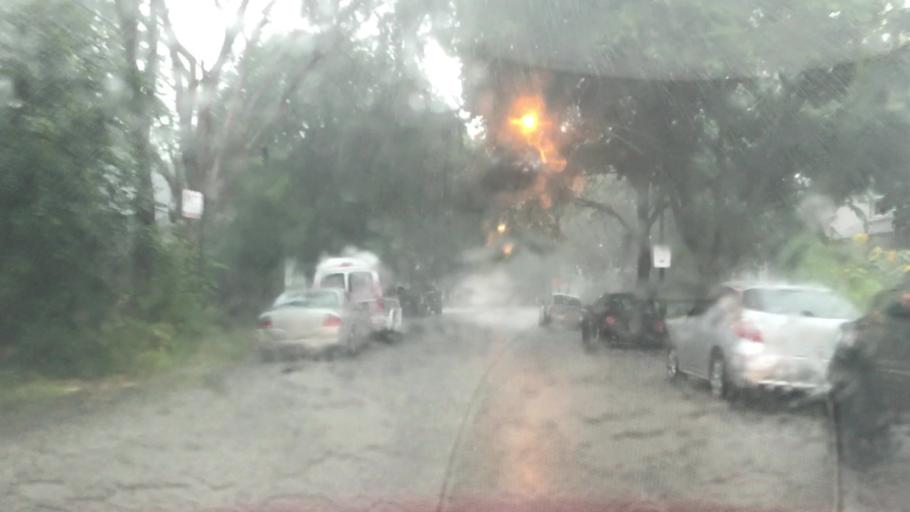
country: US
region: Illinois
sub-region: Cook County
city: Lincolnwood
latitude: 41.9654
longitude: -87.7576
